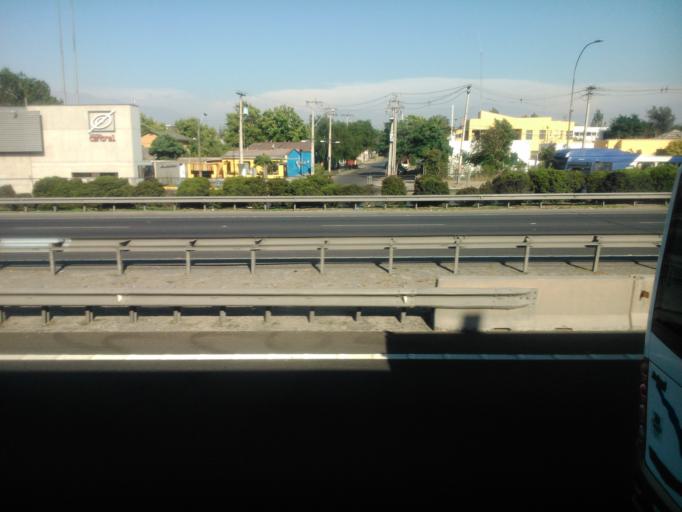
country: CL
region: Santiago Metropolitan
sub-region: Provincia de Maipo
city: San Bernardo
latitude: -33.5971
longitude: -70.7158
